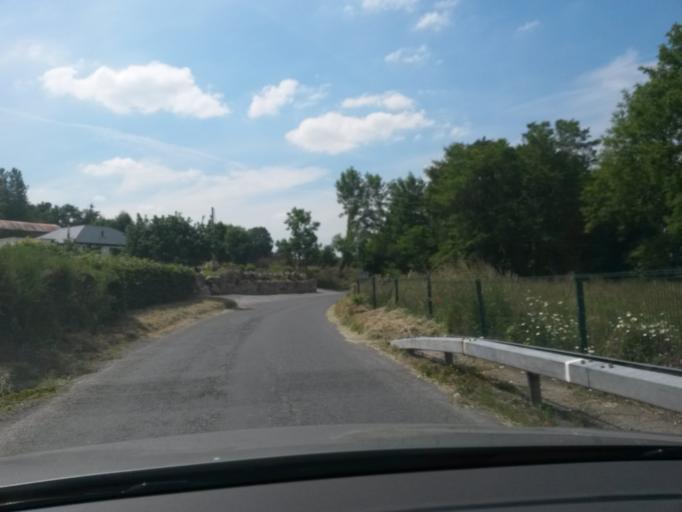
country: IE
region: Leinster
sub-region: Wicklow
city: Blessington
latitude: 53.1696
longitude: -6.5088
